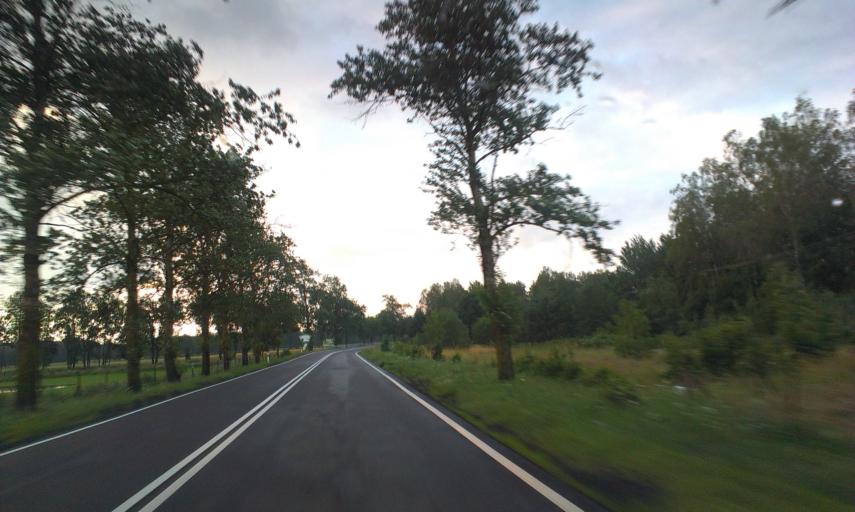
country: PL
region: West Pomeranian Voivodeship
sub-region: Powiat szczecinecki
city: Szczecinek
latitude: 53.6446
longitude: 16.7560
